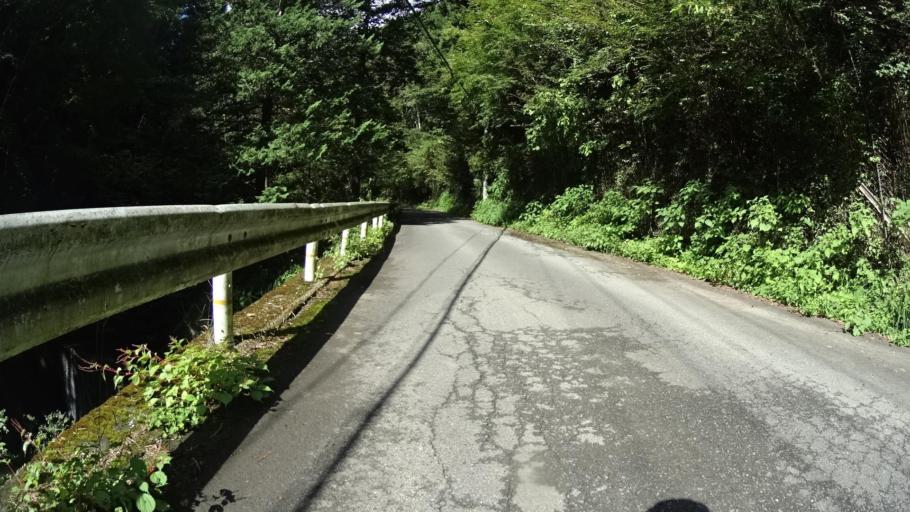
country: JP
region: Yamanashi
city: Uenohara
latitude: 35.7382
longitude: 139.0673
